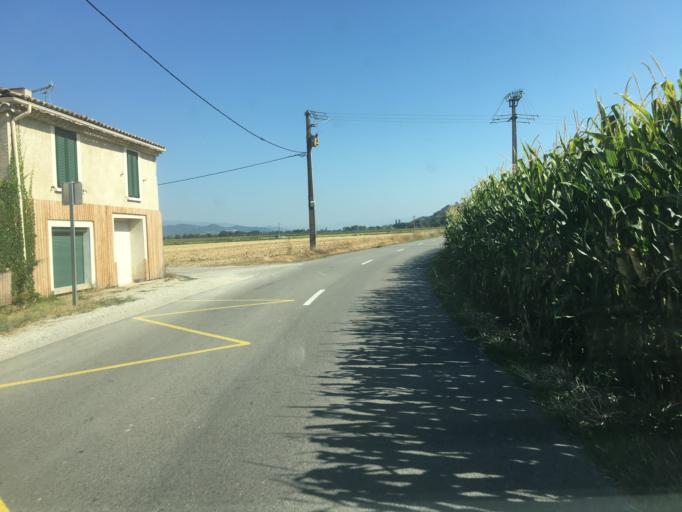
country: FR
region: Provence-Alpes-Cote d'Azur
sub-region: Departement des Alpes-de-Haute-Provence
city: Manosque
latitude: 43.8078
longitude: 5.8430
